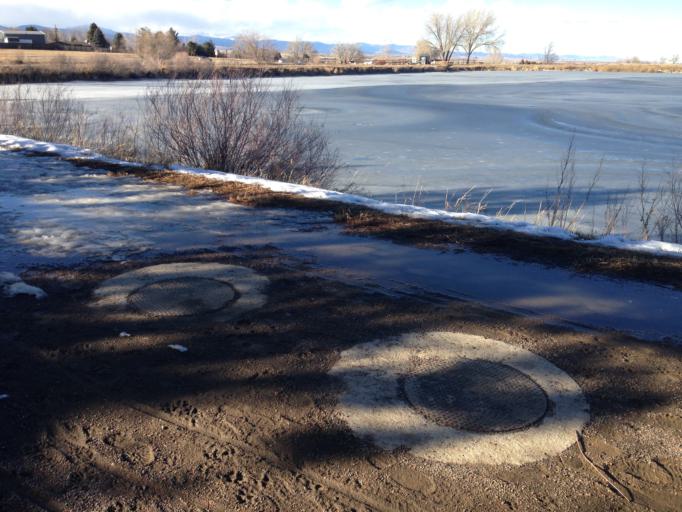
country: US
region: Colorado
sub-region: Boulder County
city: Lafayette
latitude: 40.0176
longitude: -105.1014
